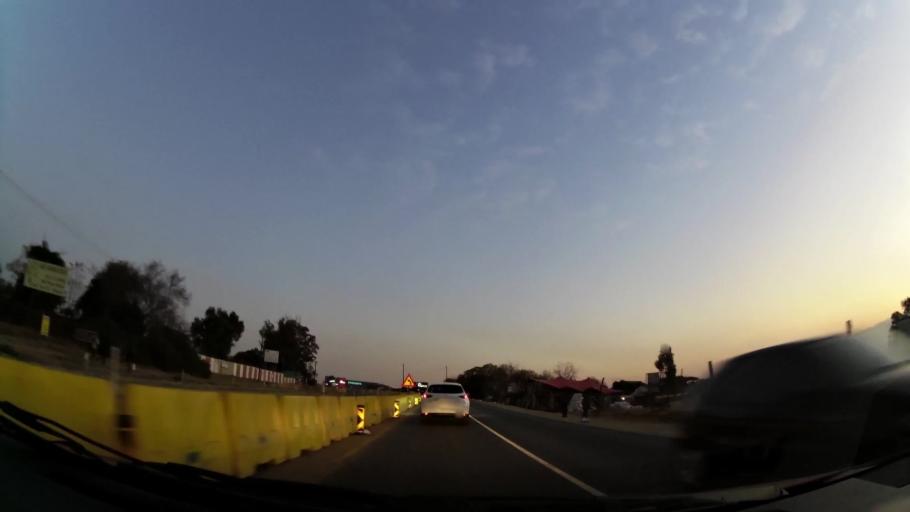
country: ZA
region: Gauteng
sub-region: City of Johannesburg Metropolitan Municipality
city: Midrand
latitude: -25.9790
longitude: 28.0771
